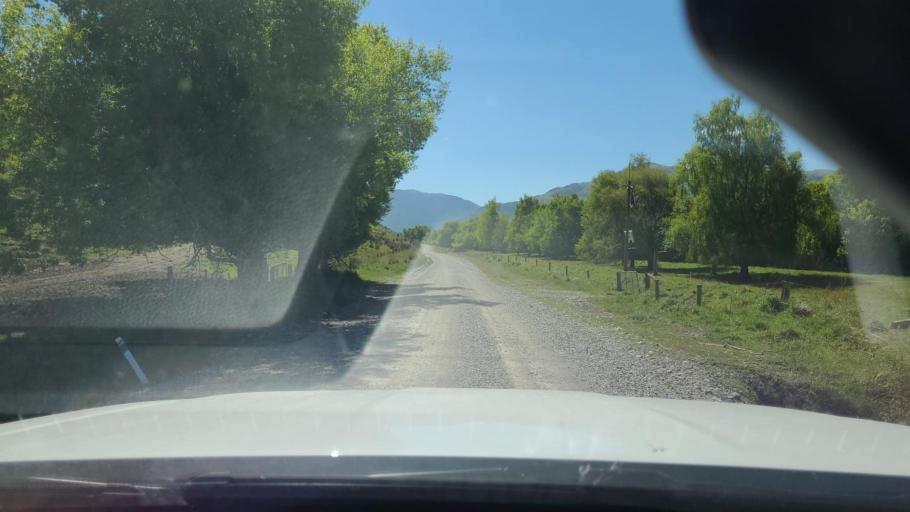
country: NZ
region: Otago
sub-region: Queenstown-Lakes District
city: Kingston
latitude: -45.7197
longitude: 168.6679
